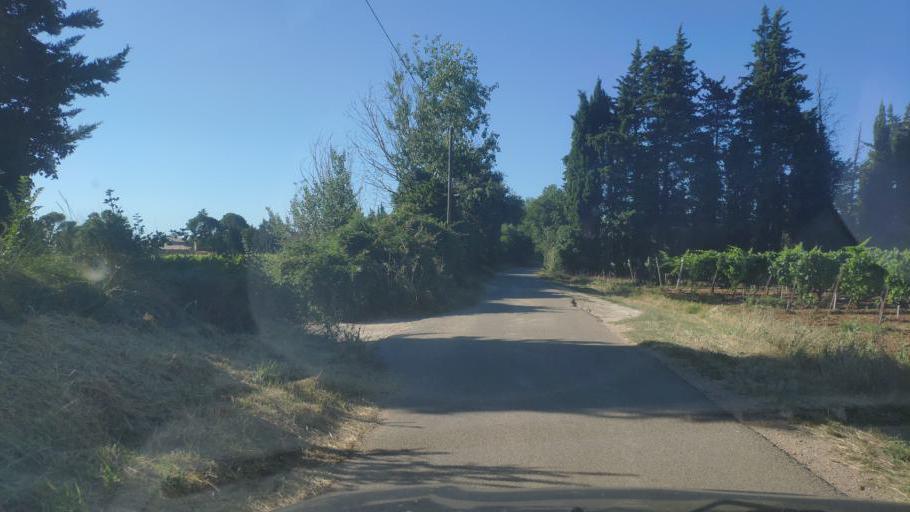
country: FR
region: Provence-Alpes-Cote d'Azur
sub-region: Departement du Vaucluse
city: Aubignan
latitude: 44.0807
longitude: 5.0453
